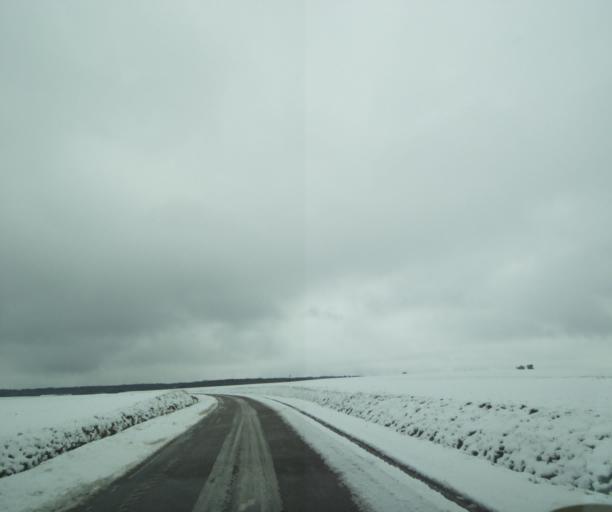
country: FR
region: Champagne-Ardenne
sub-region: Departement de la Haute-Marne
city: Laneuville-a-Remy
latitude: 48.4028
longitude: 4.8538
